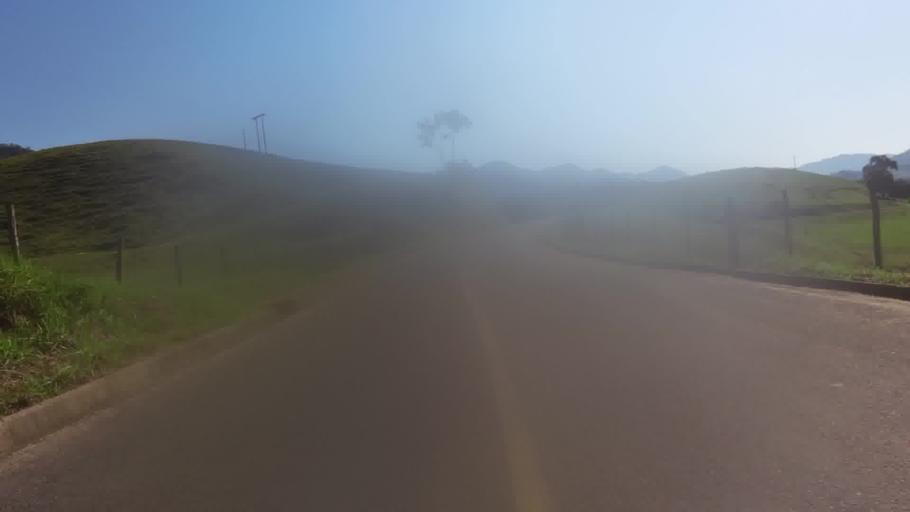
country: BR
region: Espirito Santo
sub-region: Alfredo Chaves
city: Alfredo Chaves
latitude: -20.6592
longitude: -40.7615
